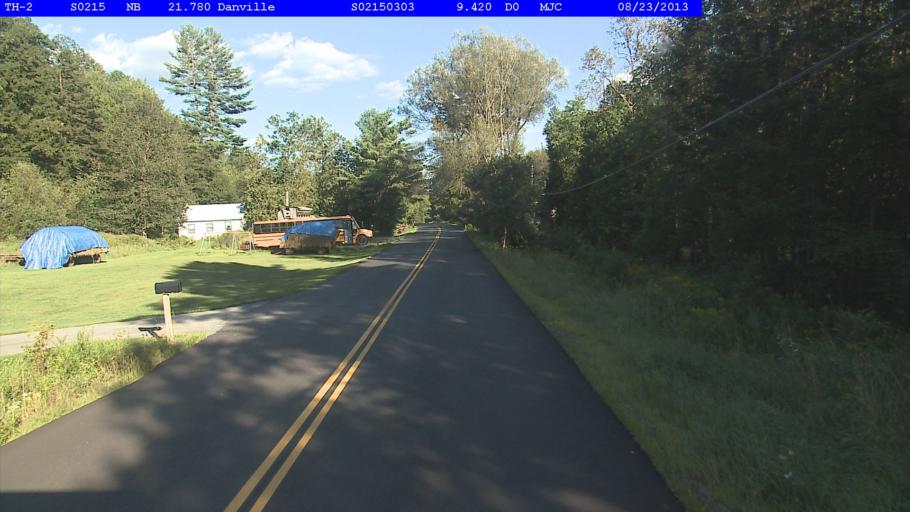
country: US
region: Vermont
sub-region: Caledonia County
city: St Johnsbury
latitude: 44.4542
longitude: -72.0756
